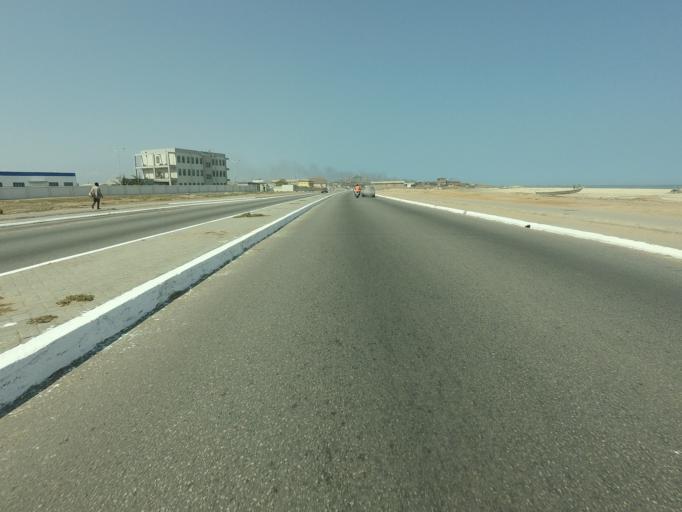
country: GH
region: Greater Accra
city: Accra
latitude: 5.5313
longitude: -0.2193
